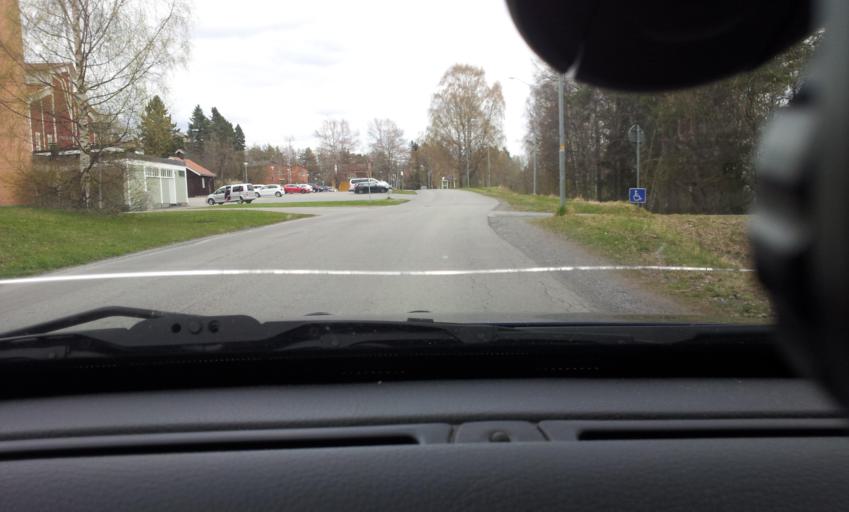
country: SE
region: Jaemtland
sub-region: OEstersunds Kommun
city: Ostersund
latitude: 63.1663
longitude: 14.5965
